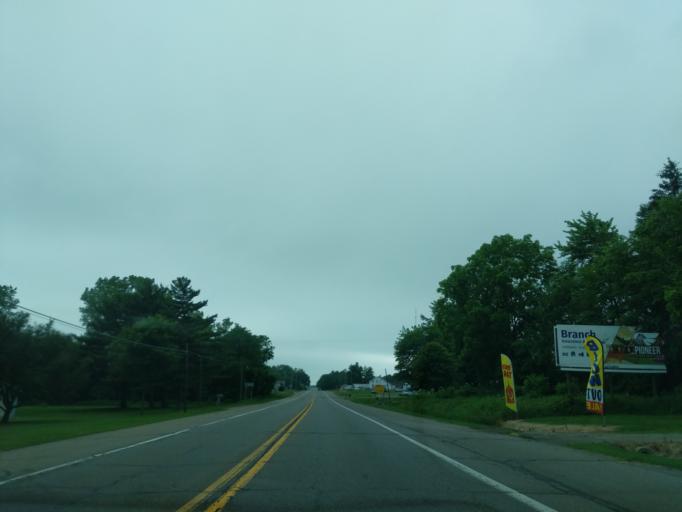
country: US
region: Michigan
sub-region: Branch County
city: Coldwater
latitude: 41.9405
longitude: -84.9427
